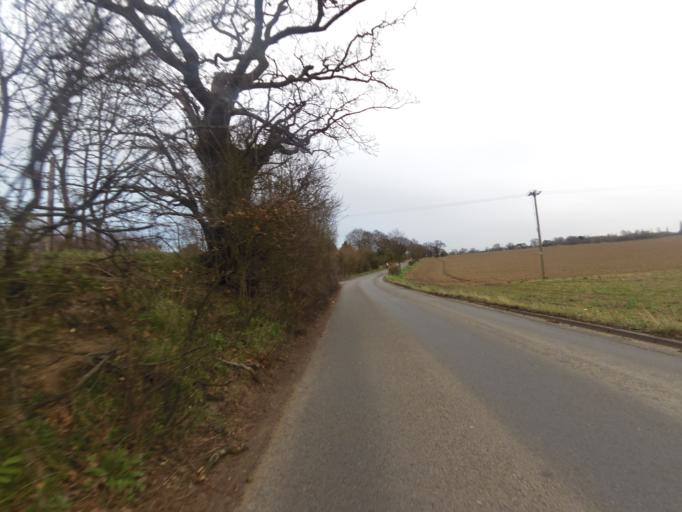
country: GB
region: England
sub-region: Suffolk
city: Ipswich
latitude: 52.0839
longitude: 1.1768
